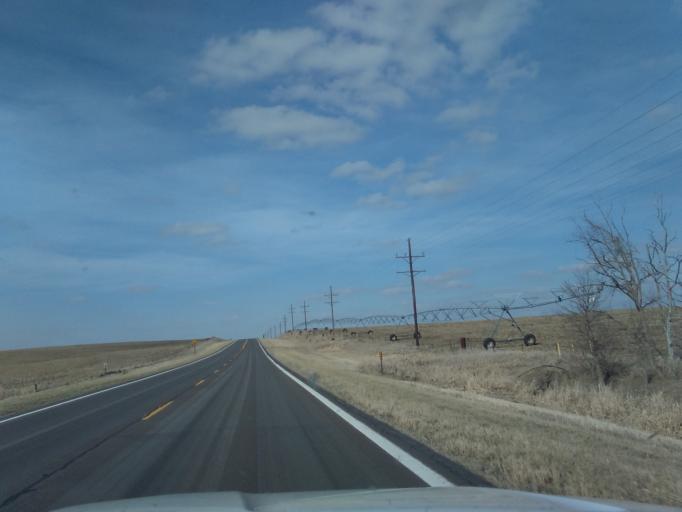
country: US
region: Nebraska
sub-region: Gage County
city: Beatrice
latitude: 40.1529
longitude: -96.9352
